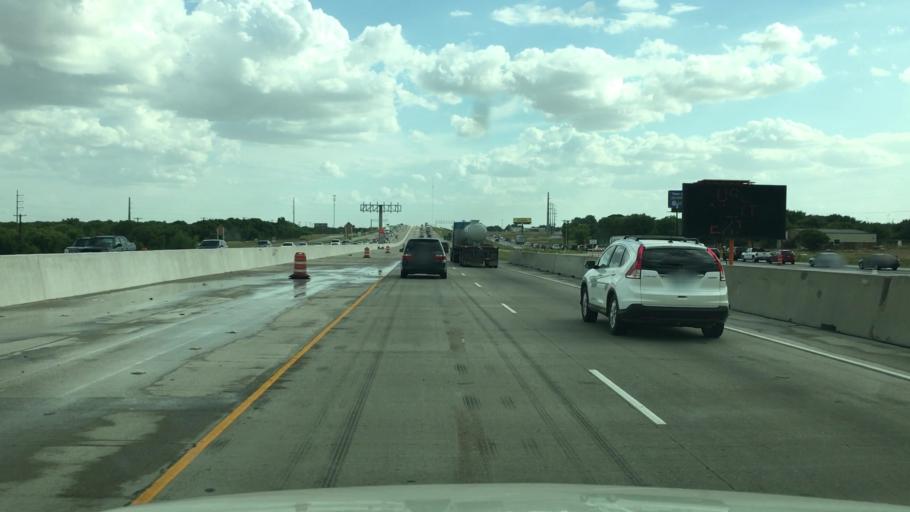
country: US
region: Texas
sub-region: McLennan County
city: Bruceville-Eddy
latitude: 31.3152
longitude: -97.2401
